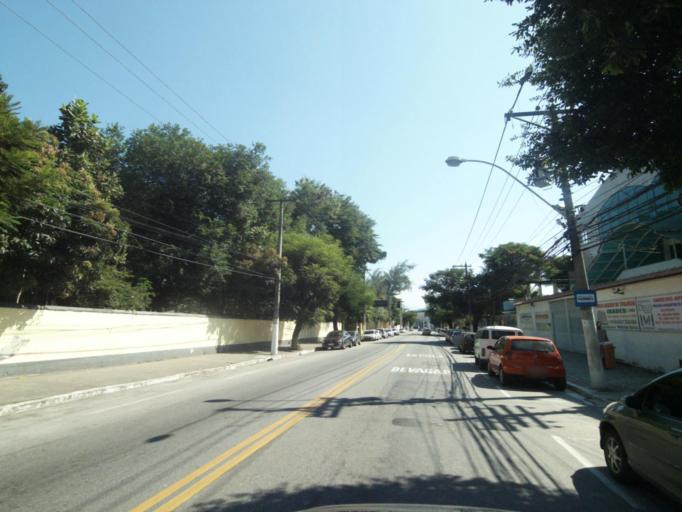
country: BR
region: Rio de Janeiro
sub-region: Niteroi
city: Niteroi
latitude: -22.8639
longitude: -43.0982
